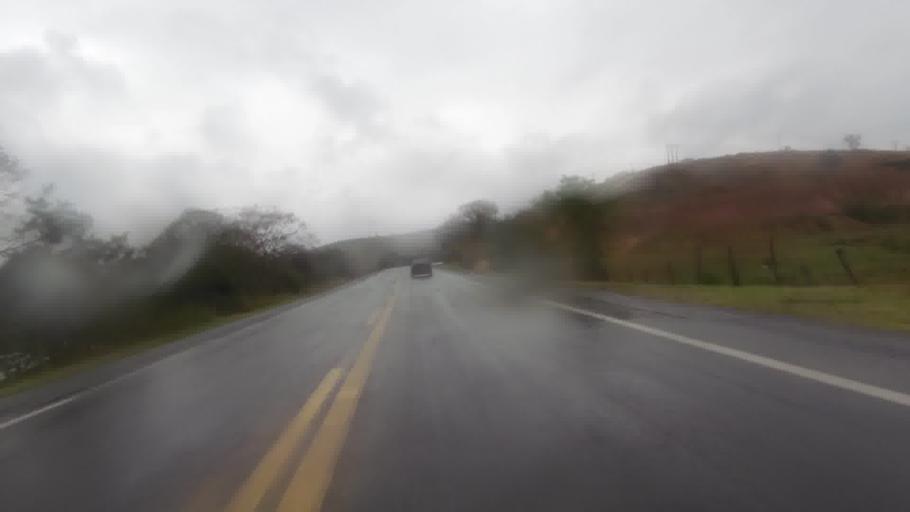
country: BR
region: Espirito Santo
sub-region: Cachoeiro De Itapemirim
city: Cachoeiro de Itapemirim
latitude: -20.9058
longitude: -41.0651
